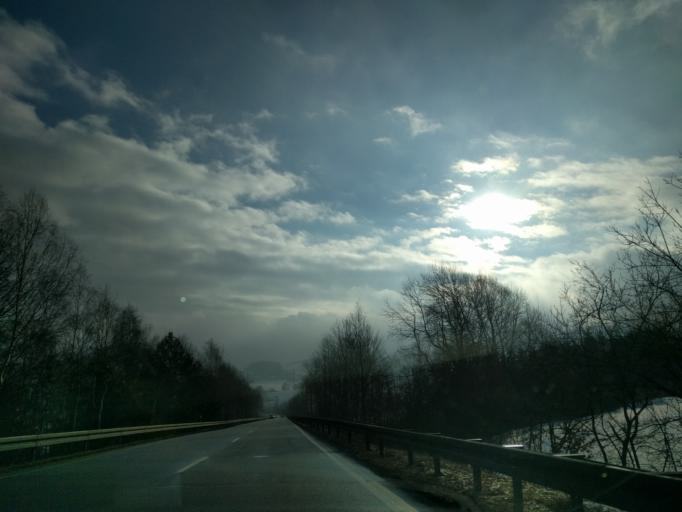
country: DE
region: Bavaria
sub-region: Lower Bavaria
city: Zwiesel
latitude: 49.0069
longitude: 13.2334
